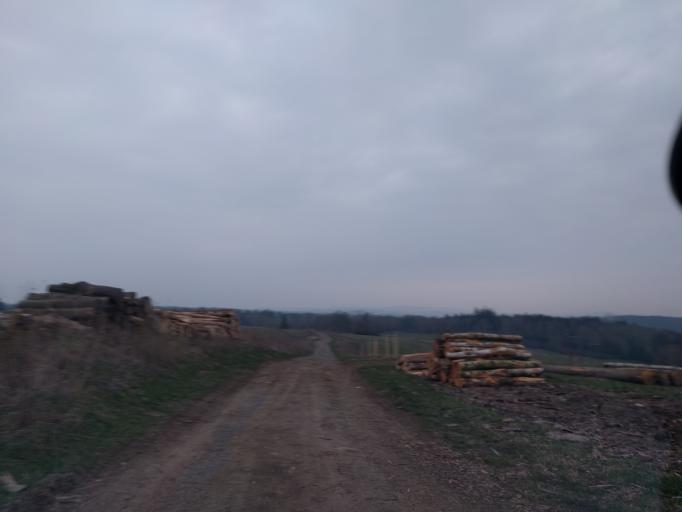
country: CZ
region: Karlovarsky
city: Bochov
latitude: 50.0996
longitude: 13.0966
